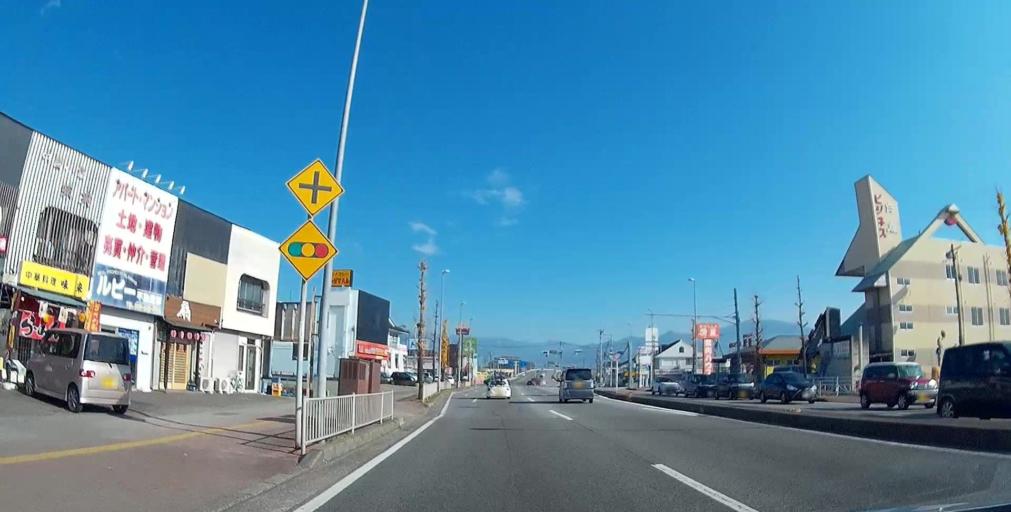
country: JP
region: Yamanashi
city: Isawa
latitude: 35.6438
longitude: 138.6333
